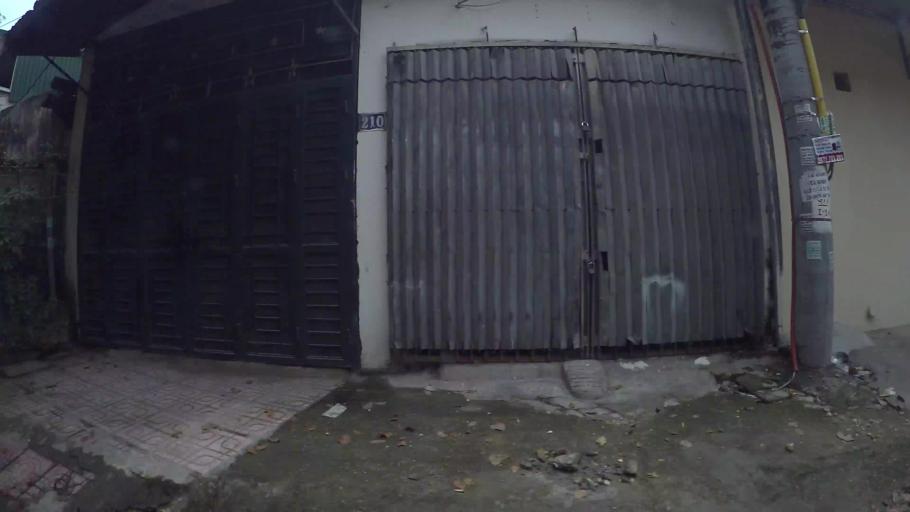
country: VN
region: Ha Noi
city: Van Dien
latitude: 20.9773
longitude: 105.8534
